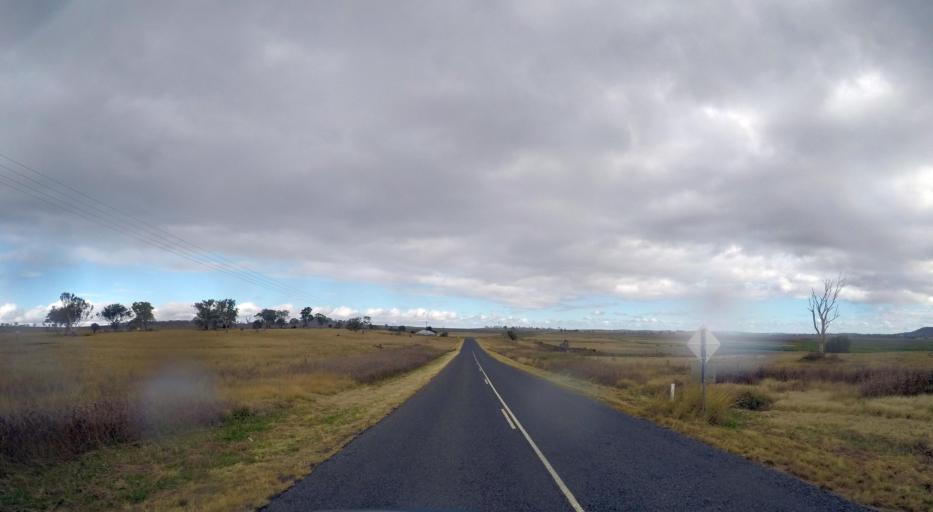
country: AU
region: Queensland
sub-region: Southern Downs
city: Warwick
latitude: -28.0458
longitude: 152.0449
